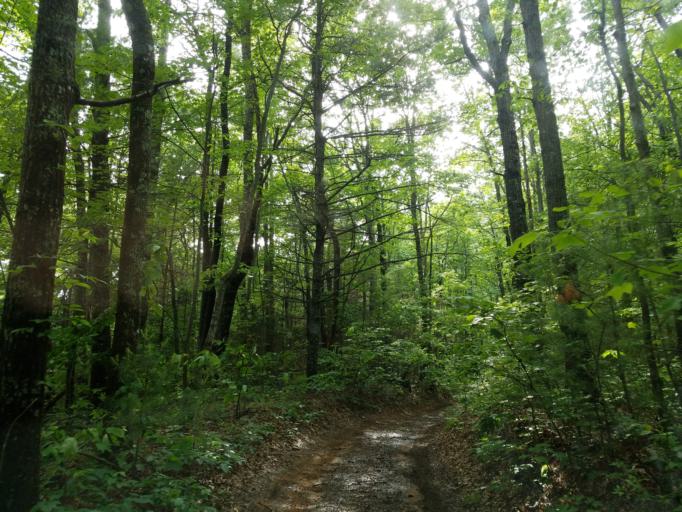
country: US
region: Georgia
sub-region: Union County
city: Blairsville
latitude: 34.7332
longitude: -84.0231
